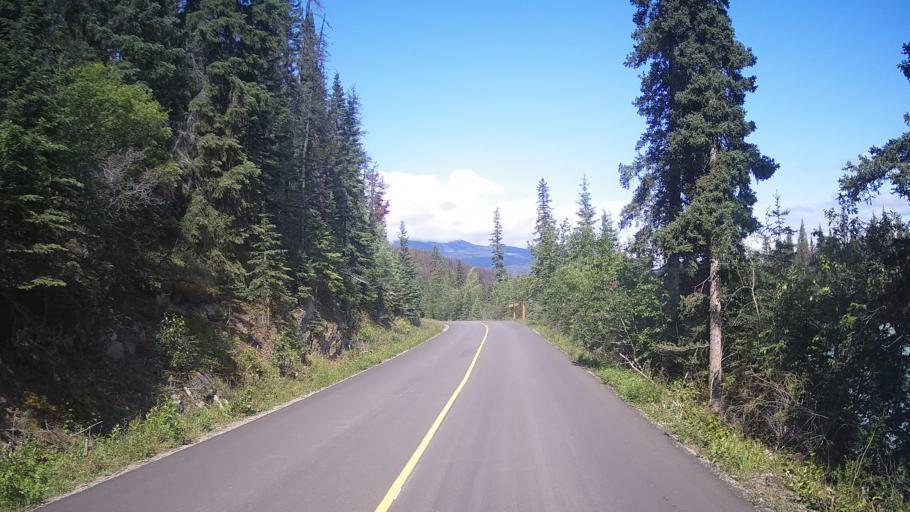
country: CA
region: Alberta
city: Jasper Park Lodge
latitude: 52.7409
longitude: -117.9632
